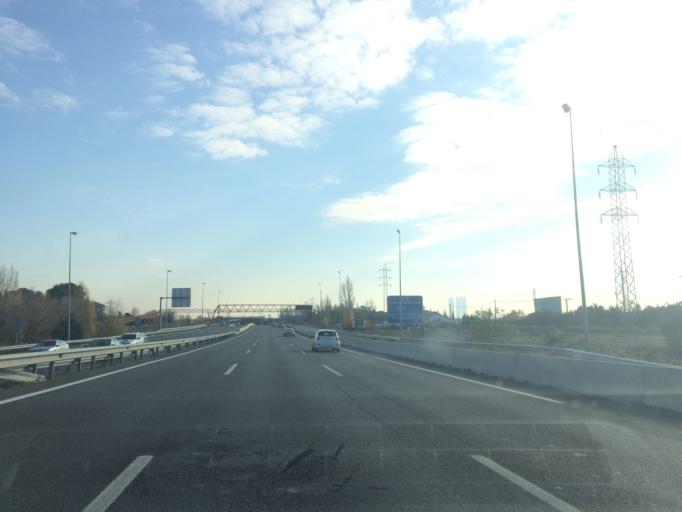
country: ES
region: Madrid
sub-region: Provincia de Madrid
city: Las Tablas
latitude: 40.5314
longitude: -3.6940
